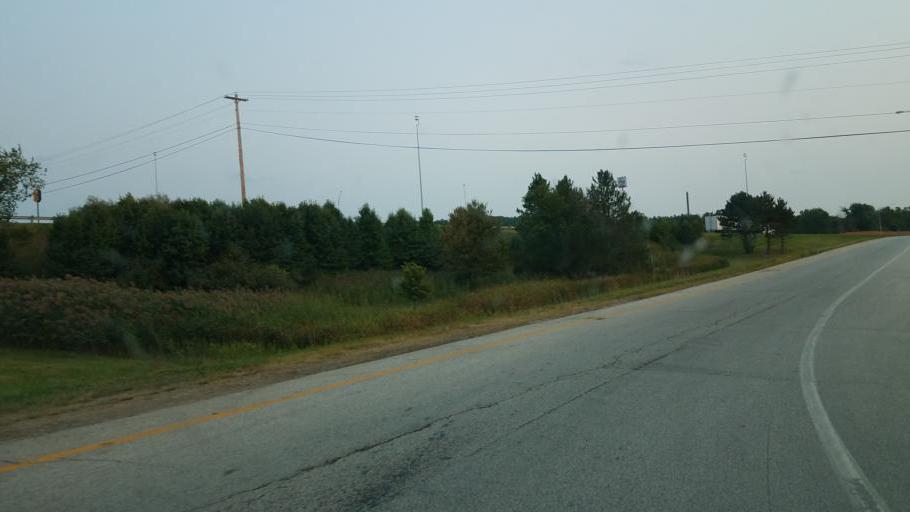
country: US
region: Ohio
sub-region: Medina County
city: Medina
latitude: 41.1360
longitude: -81.7959
